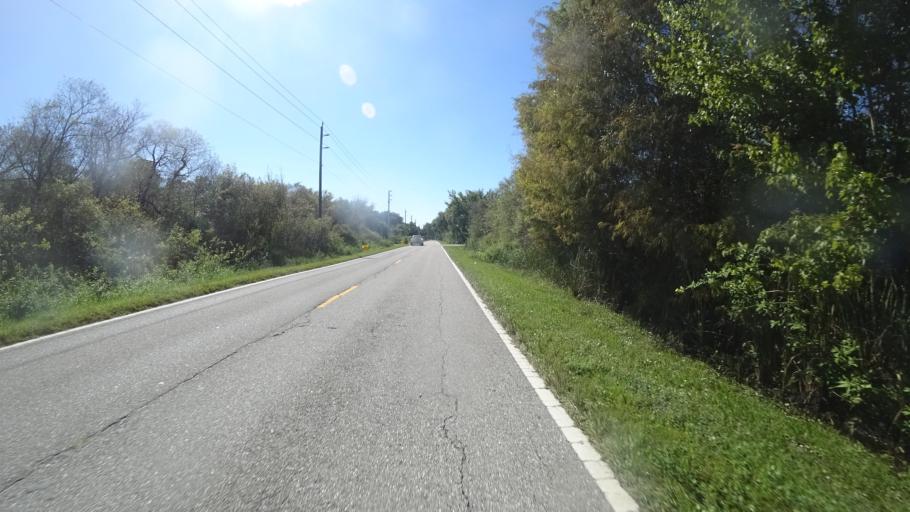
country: US
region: Florida
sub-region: Sarasota County
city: Lake Sarasota
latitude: 27.3285
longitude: -82.2695
